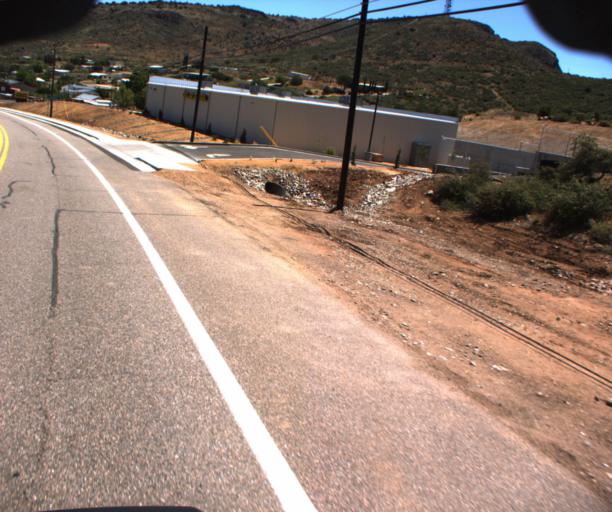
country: US
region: Arizona
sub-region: Yavapai County
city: Congress
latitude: 34.2169
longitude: -112.7516
